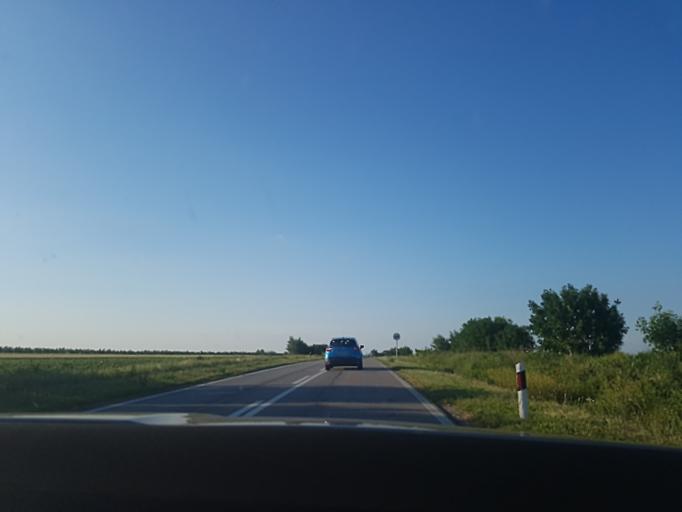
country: RS
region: Autonomna Pokrajina Vojvodina
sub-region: Juznobanatski Okrug
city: Vrsac
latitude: 45.1625
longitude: 21.2911
